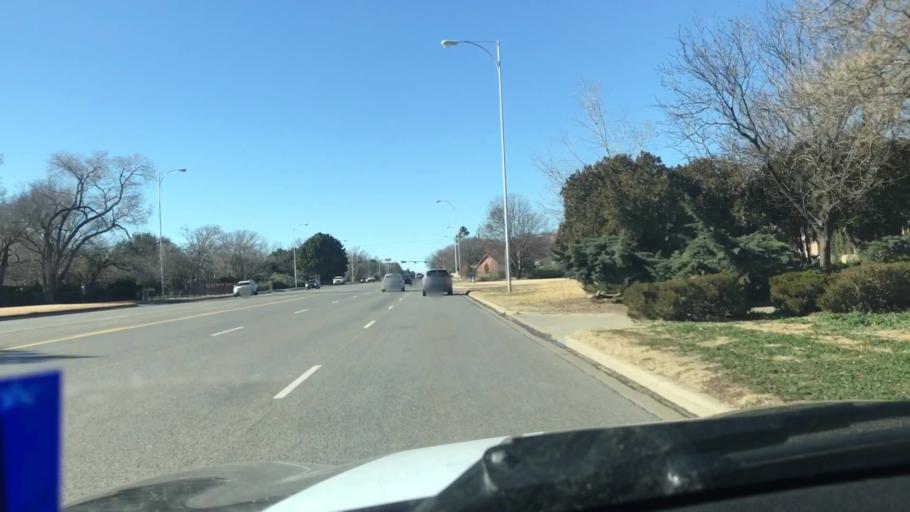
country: US
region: Texas
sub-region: Lubbock County
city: Lubbock
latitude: 33.5779
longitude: -101.9196
